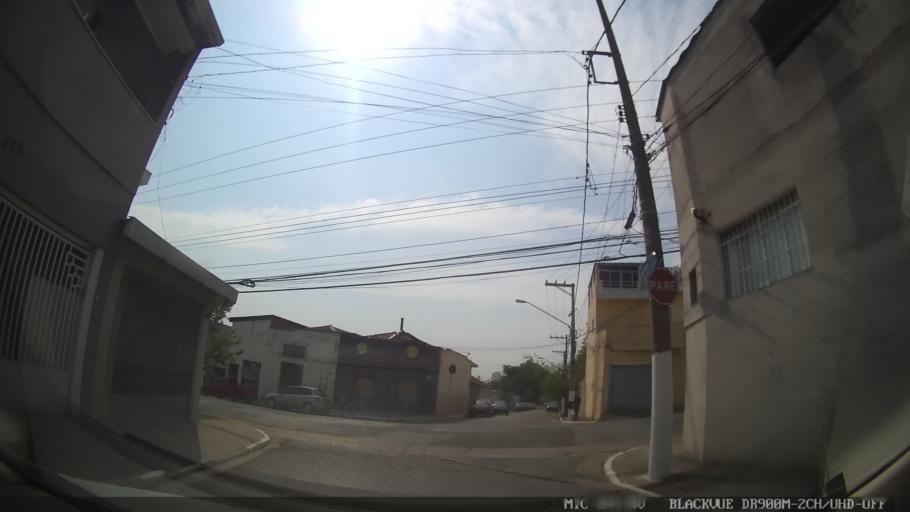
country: BR
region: Sao Paulo
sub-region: Sao Caetano Do Sul
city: Sao Caetano do Sul
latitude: -23.6131
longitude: -46.6054
